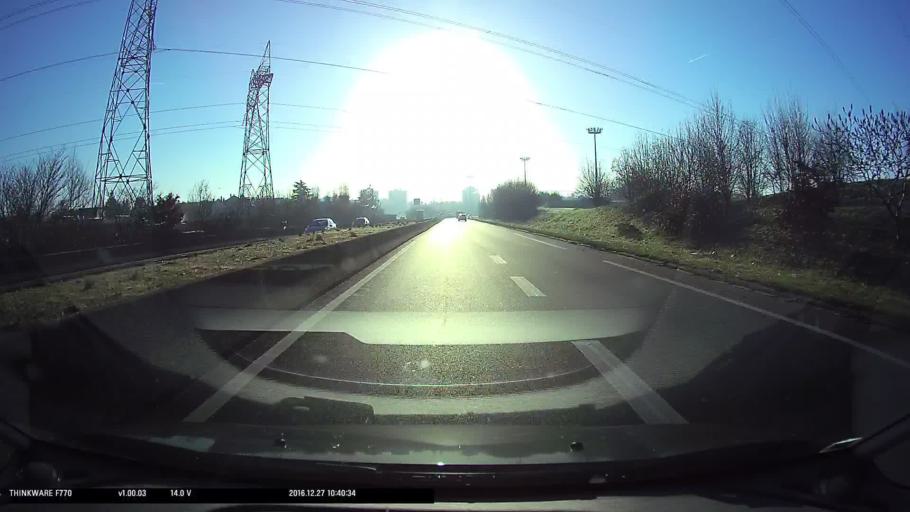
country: FR
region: Ile-de-France
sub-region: Departement du Val-d'Oise
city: Ennery
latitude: 49.0681
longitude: 2.0845
